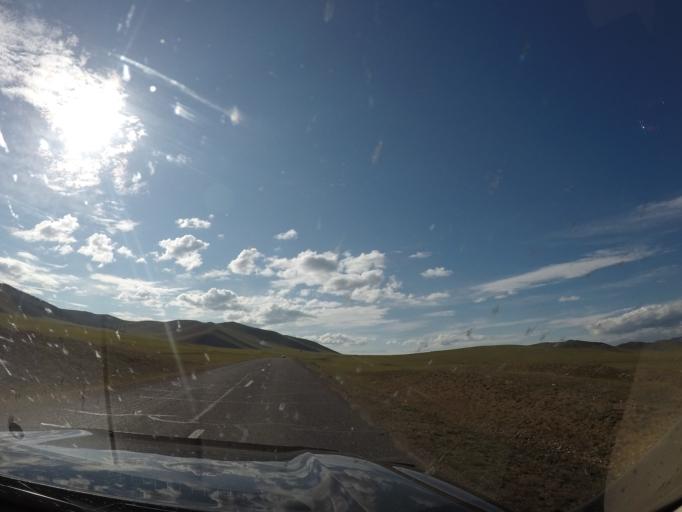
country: MN
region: Hentiy
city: Modot
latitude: 47.7454
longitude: 108.9805
